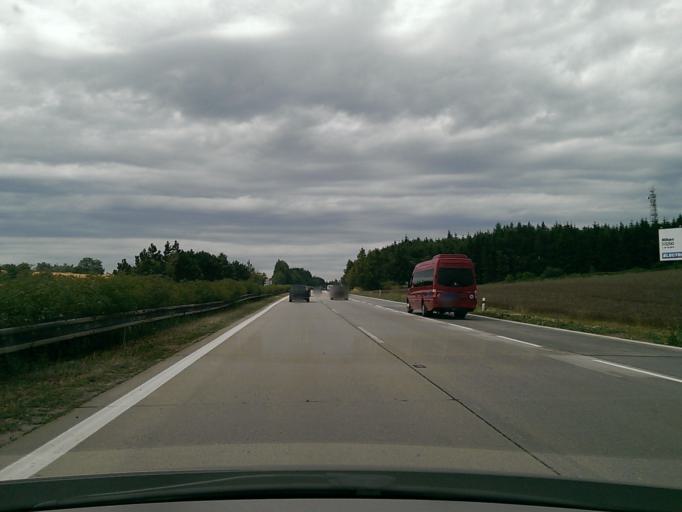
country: CZ
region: Vysocina
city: Kamenice
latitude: 49.4073
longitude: 15.7904
